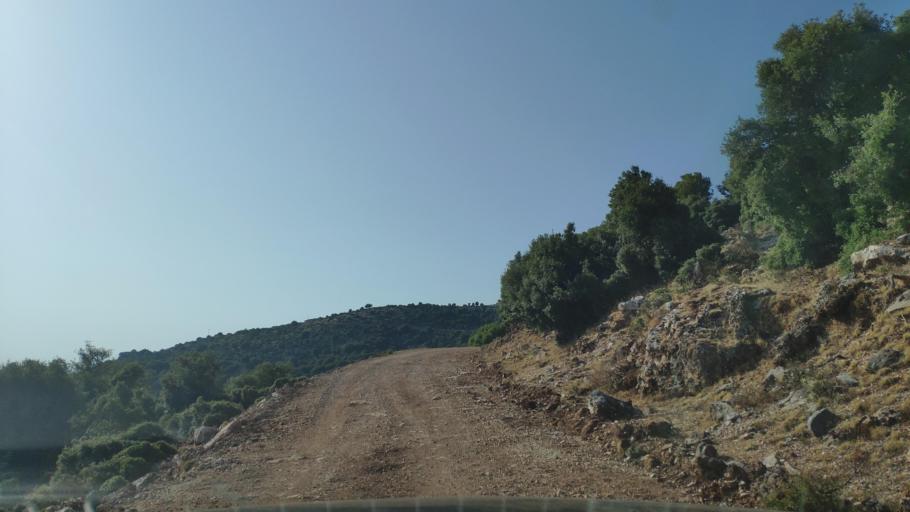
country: GR
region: West Greece
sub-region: Nomos Aitolias kai Akarnanias
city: Monastirakion
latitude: 38.8348
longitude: 20.9710
